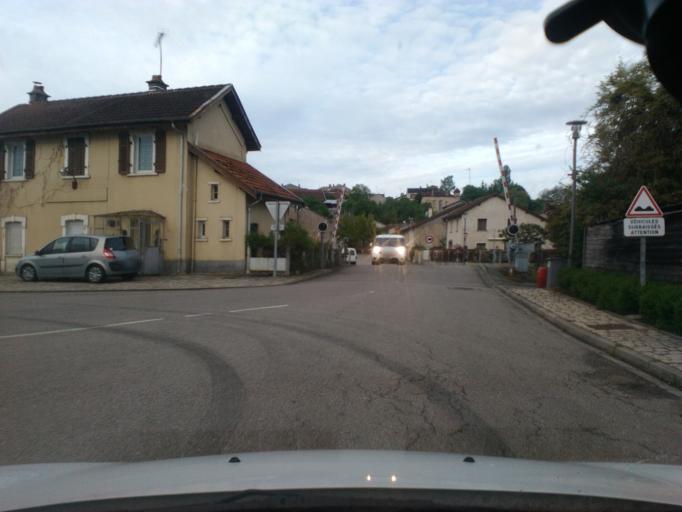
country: FR
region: Lorraine
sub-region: Departement des Vosges
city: Mirecourt
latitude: 48.3229
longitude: 6.1269
